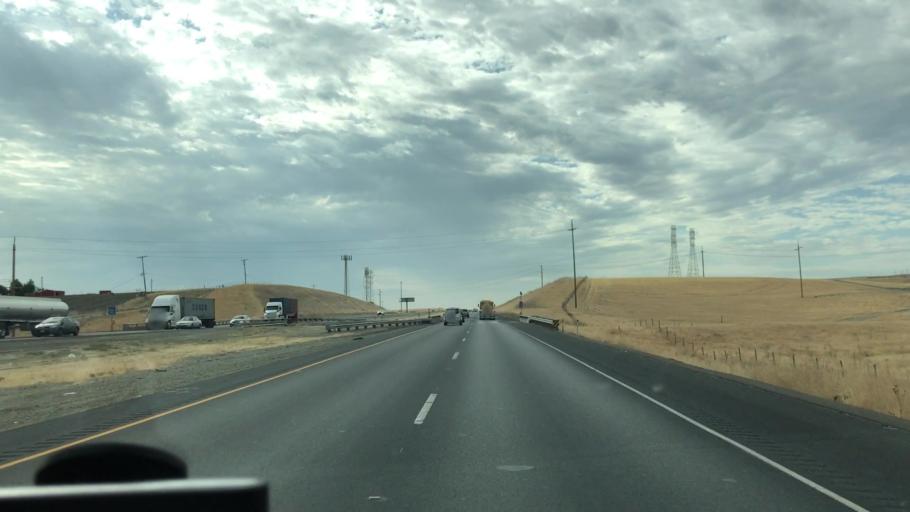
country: US
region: California
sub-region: San Joaquin County
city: Mountain House
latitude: 37.7069
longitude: -121.5149
